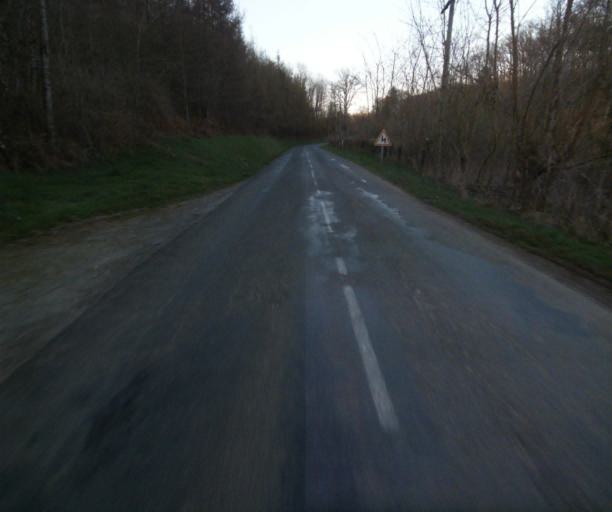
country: FR
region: Limousin
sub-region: Departement de la Correze
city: Saint-Clement
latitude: 45.3446
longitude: 1.6231
